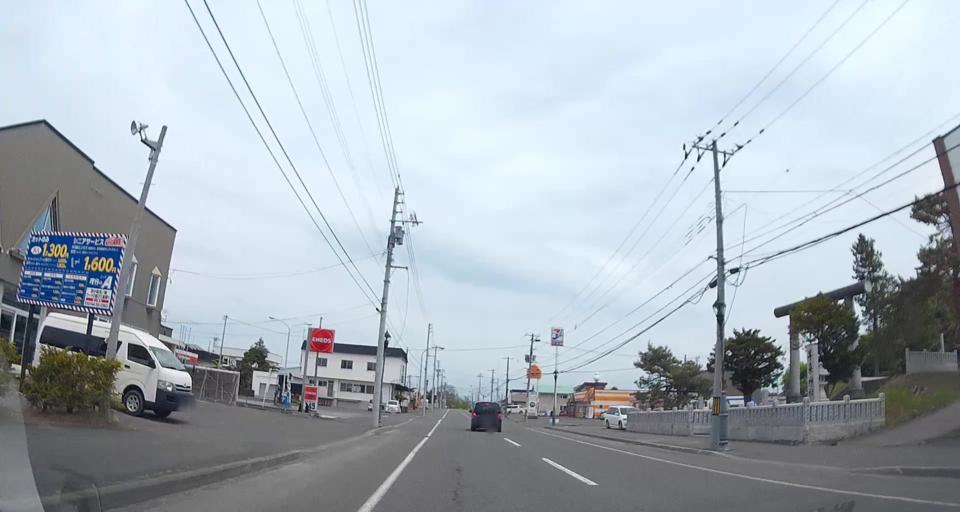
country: JP
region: Hokkaido
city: Chitose
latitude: 42.7665
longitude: 141.8187
